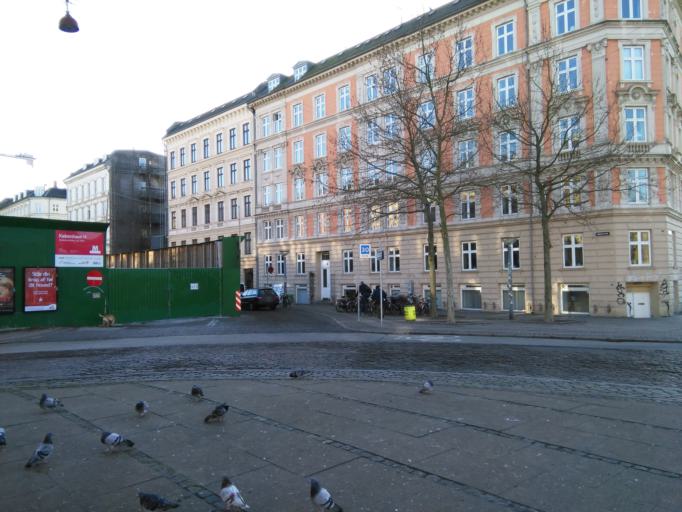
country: DK
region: Capital Region
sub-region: Kobenhavn
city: Copenhagen
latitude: 55.6708
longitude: 12.5617
